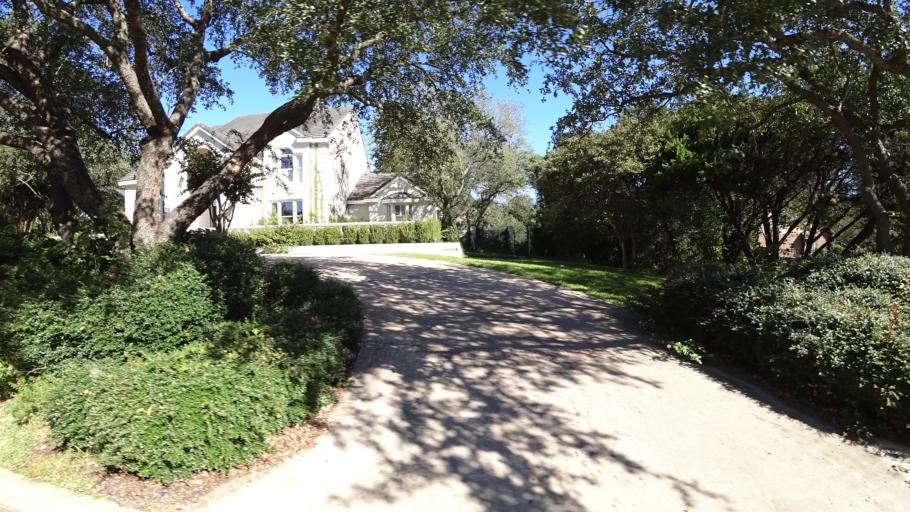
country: US
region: Texas
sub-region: Travis County
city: West Lake Hills
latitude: 30.3317
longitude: -97.7852
